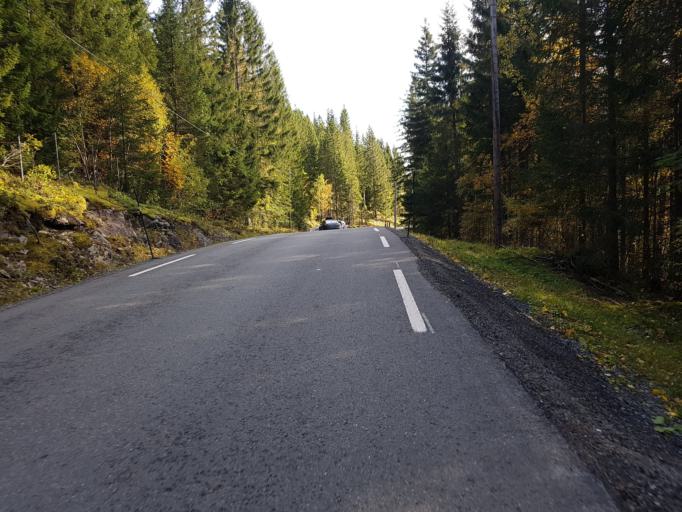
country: NO
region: Sor-Trondelag
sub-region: Malvik
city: Malvik
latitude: 63.3622
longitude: 10.6288
